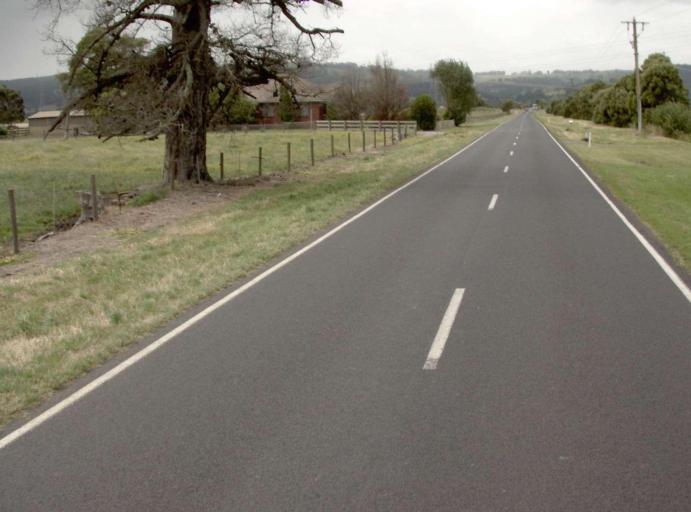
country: AU
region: Victoria
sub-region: Latrobe
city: Moe
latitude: -38.1812
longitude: 146.1470
